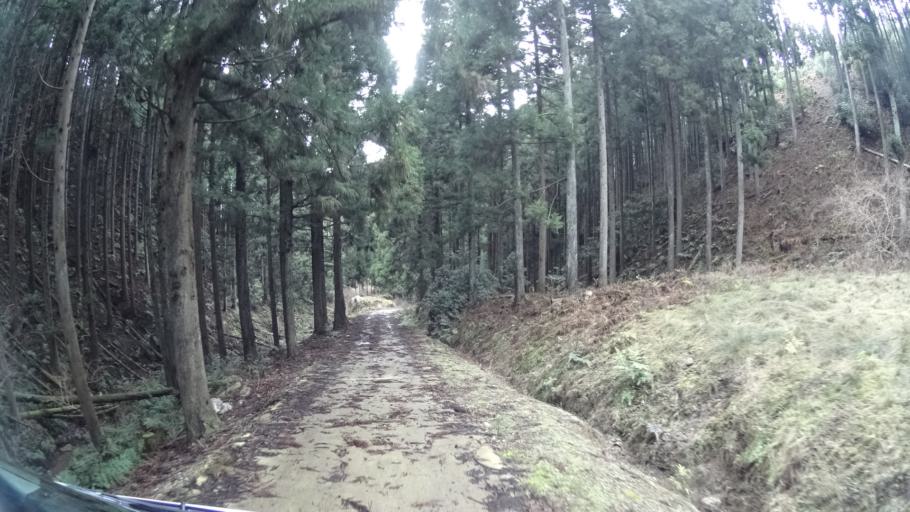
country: JP
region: Kyoto
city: Ayabe
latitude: 35.3080
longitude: 135.3772
